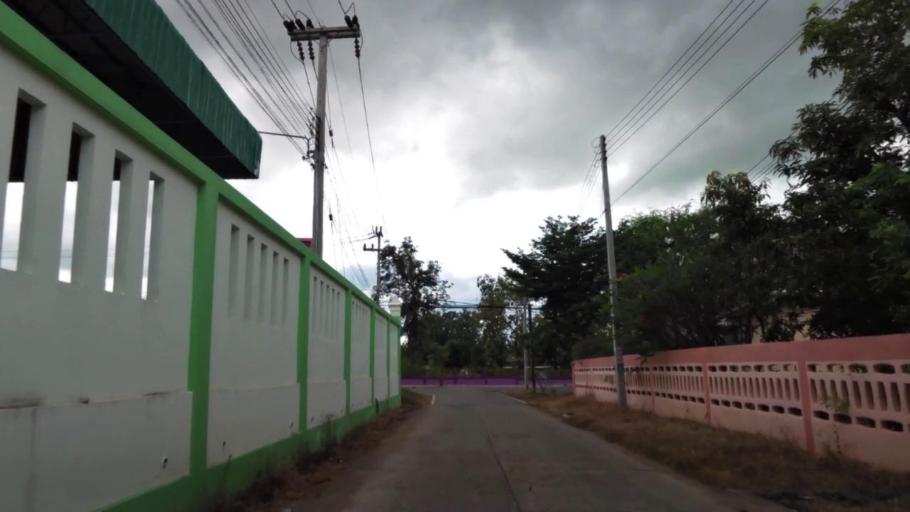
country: TH
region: Nakhon Sawan
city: Phai Sali
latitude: 15.5999
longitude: 100.6563
